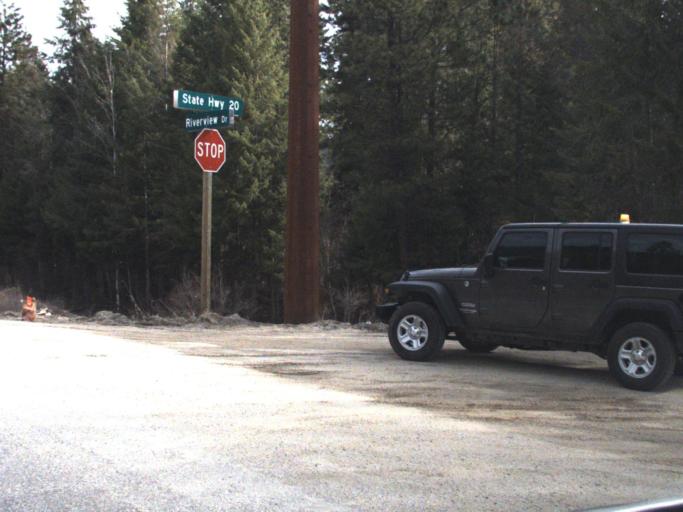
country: US
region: Washington
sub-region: Pend Oreille County
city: Newport
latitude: 48.4882
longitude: -117.2691
